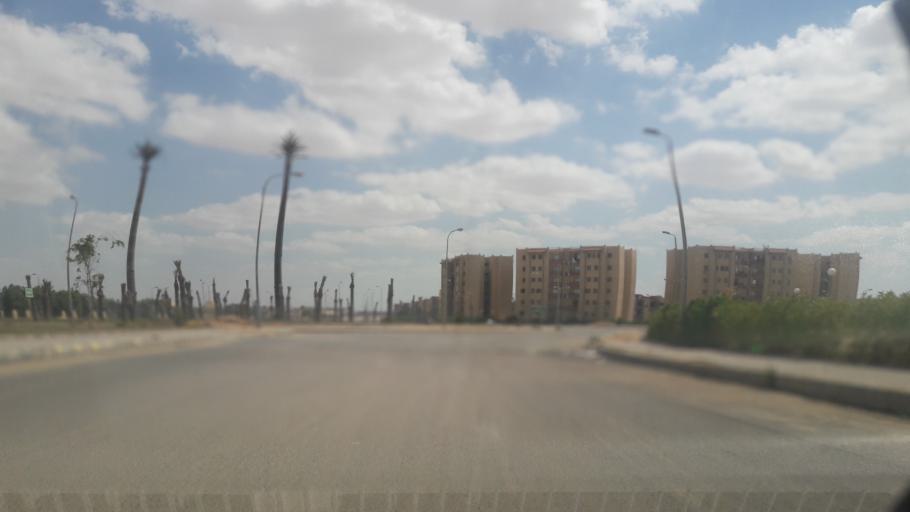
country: EG
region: Al Jizah
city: Madinat Sittah Uktubar
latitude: 29.9360
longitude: 31.0652
